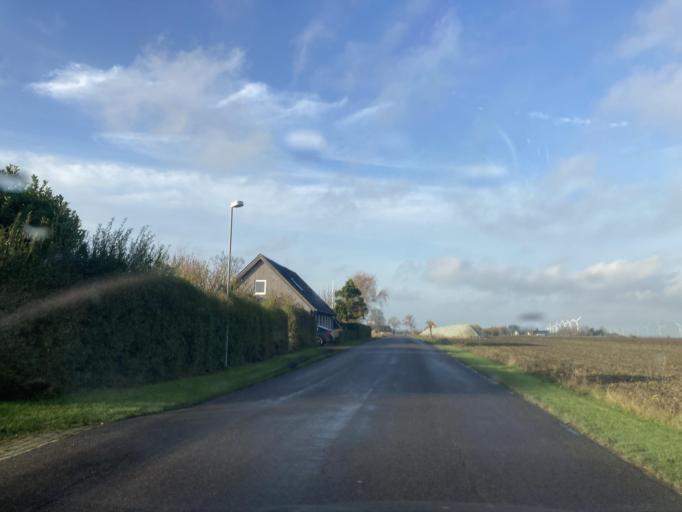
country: DK
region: Zealand
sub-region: Lolland Kommune
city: Rodby
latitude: 54.6890
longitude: 11.3800
